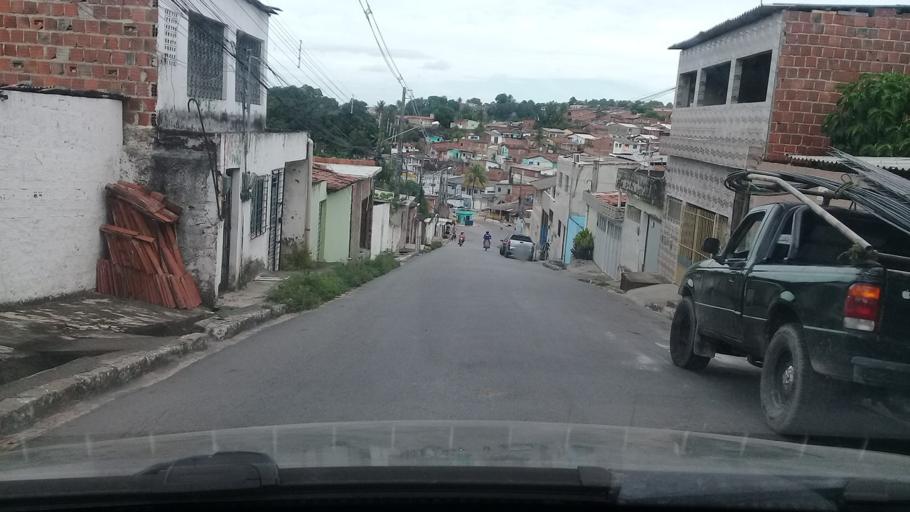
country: BR
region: Pernambuco
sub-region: Jaboatao Dos Guararapes
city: Jaboatao dos Guararapes
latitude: -8.1132
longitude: -34.9593
